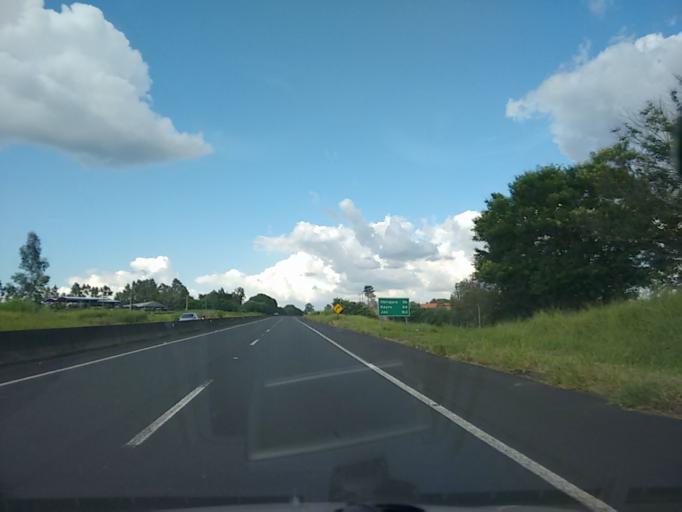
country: BR
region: Sao Paulo
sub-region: Marilia
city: Marilia
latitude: -22.2288
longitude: -49.8069
